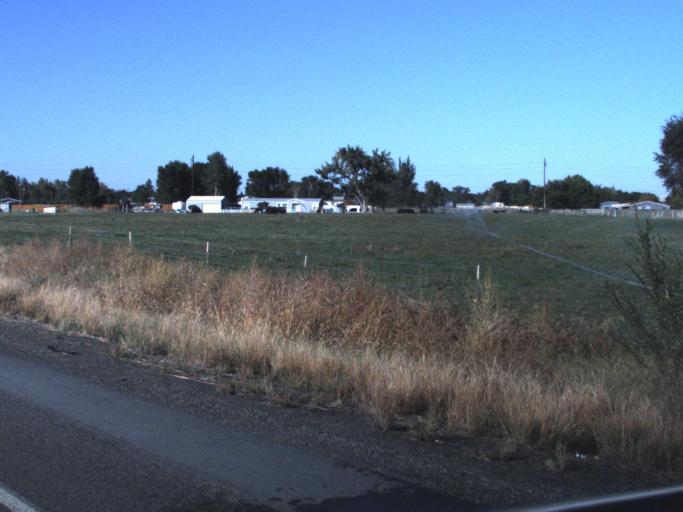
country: US
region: Washington
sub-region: Benton County
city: Finley
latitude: 46.1547
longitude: -119.0318
